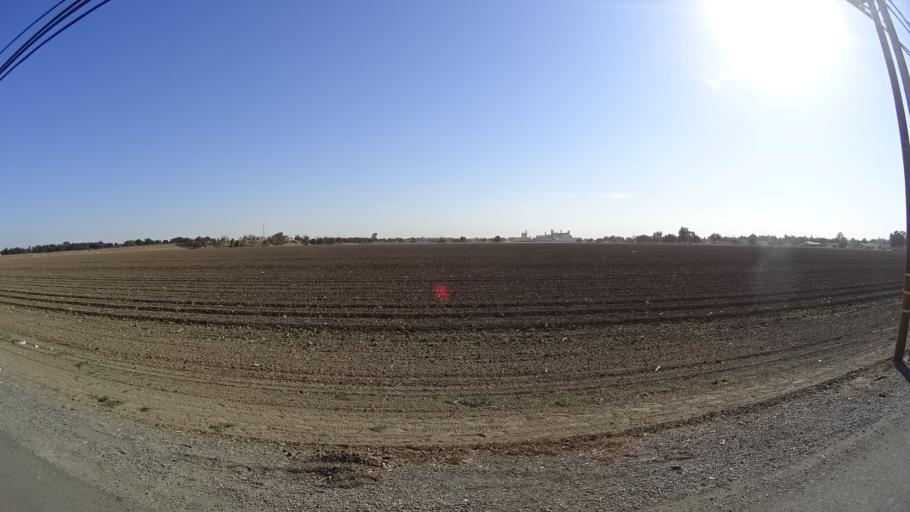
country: US
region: California
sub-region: Yolo County
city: Woodland
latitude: 38.6960
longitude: -121.7839
